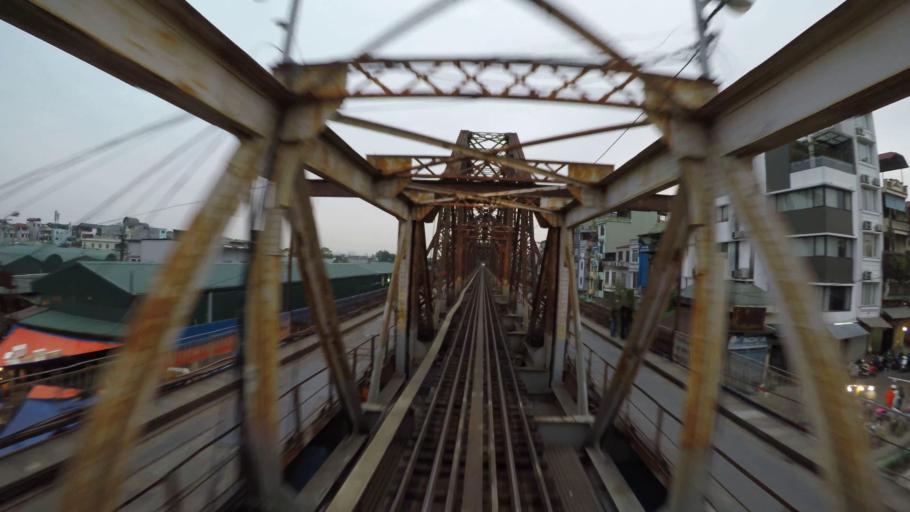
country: VN
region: Ha Noi
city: Hoan Kiem
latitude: 21.0476
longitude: 105.8693
